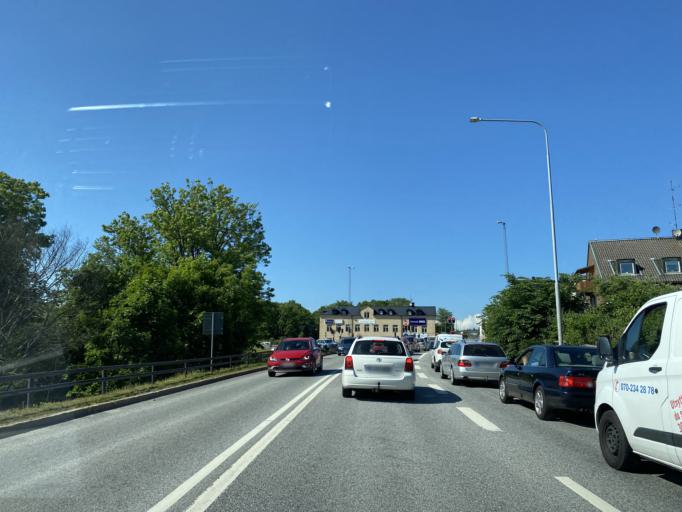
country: SE
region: Stockholm
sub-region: Norrtalje Kommun
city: Norrtalje
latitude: 59.7580
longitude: 18.6969
